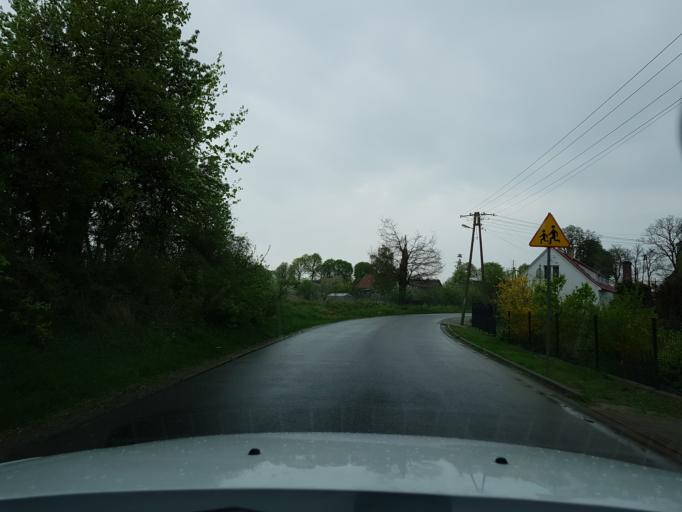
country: PL
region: West Pomeranian Voivodeship
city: Trzcinsko Zdroj
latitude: 52.9078
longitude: 14.6510
